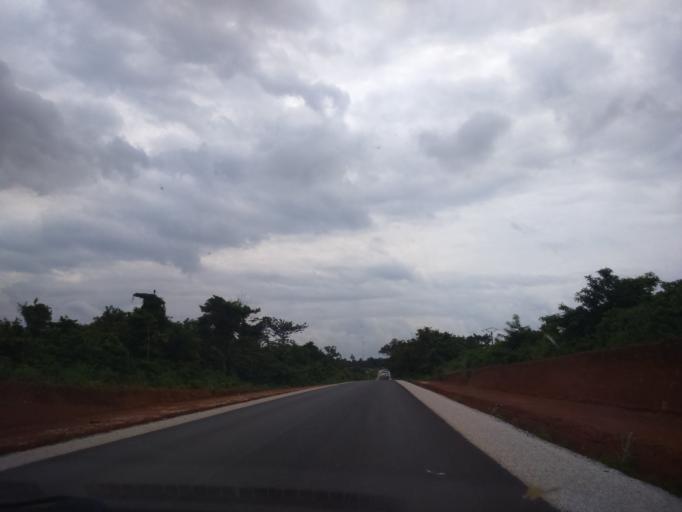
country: CI
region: Lagunes
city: Akoupe
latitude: 6.3325
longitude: -3.8467
